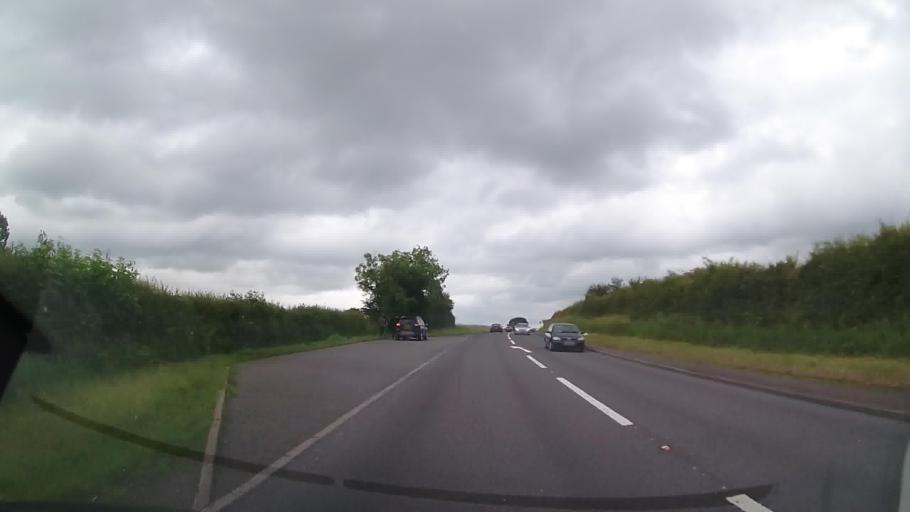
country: GB
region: England
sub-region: Shropshire
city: Stoke upon Tern
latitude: 52.8910
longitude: -2.5338
